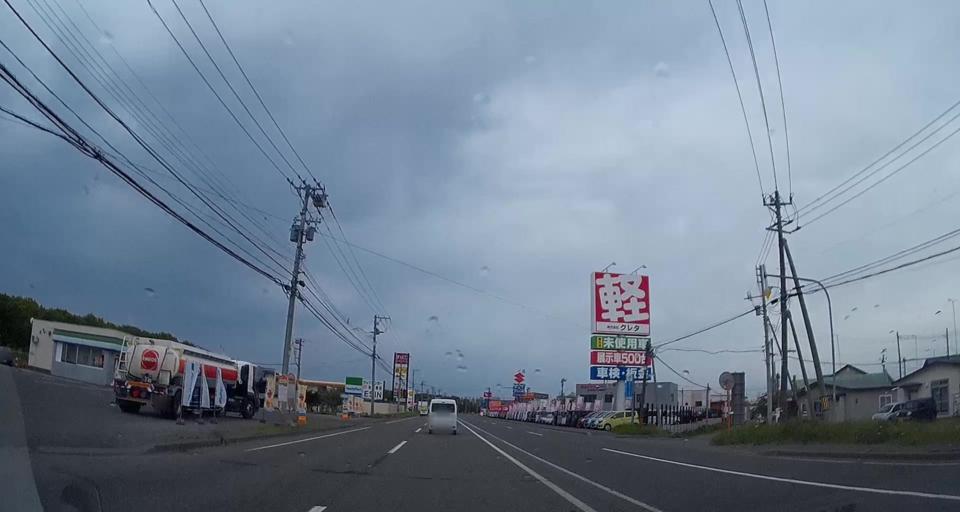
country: JP
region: Hokkaido
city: Tomakomai
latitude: 42.6732
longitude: 141.7057
